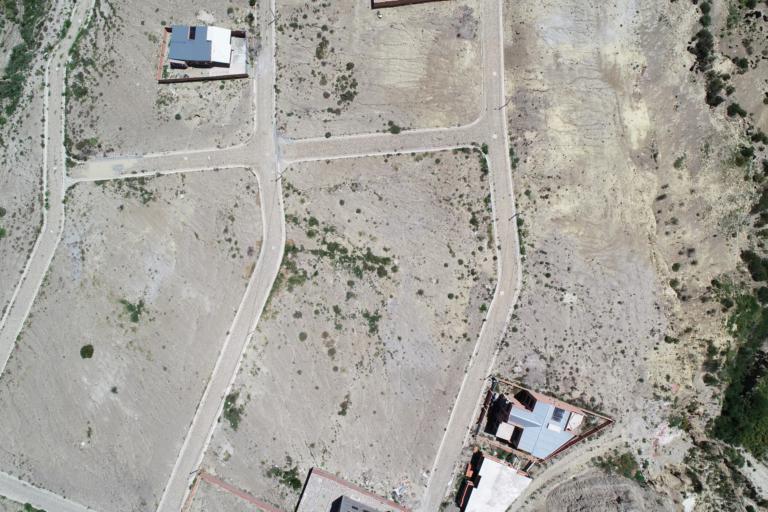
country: BO
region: La Paz
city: La Paz
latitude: -16.5217
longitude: -68.0508
